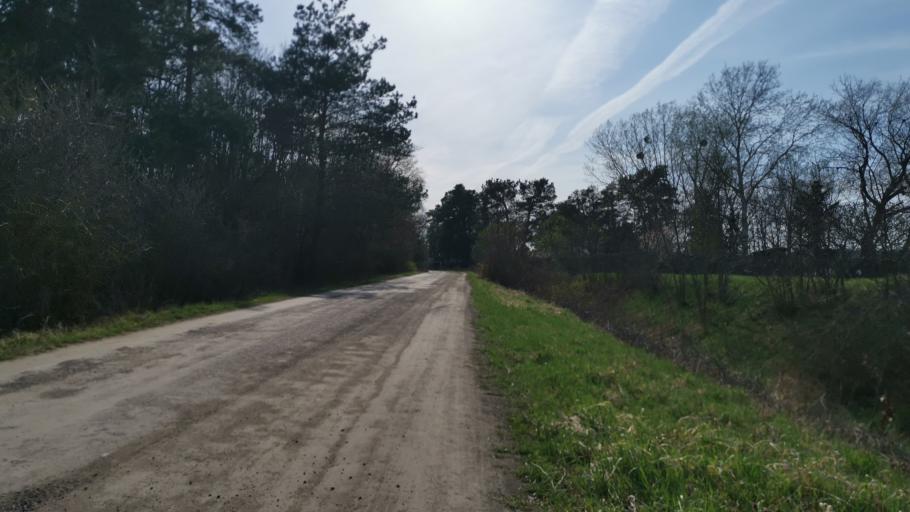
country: CZ
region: South Moravian
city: Tvrdonice
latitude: 48.7257
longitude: 17.0326
